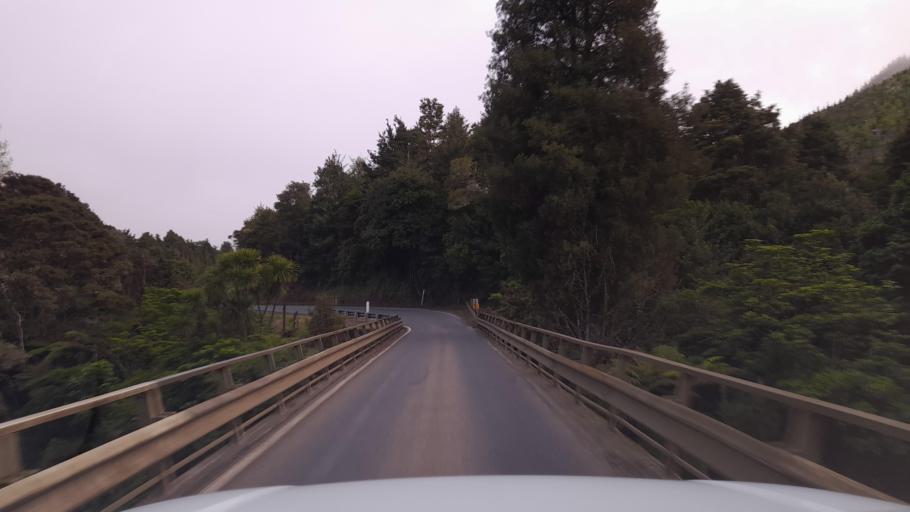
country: NZ
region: Northland
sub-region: Far North District
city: Moerewa
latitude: -35.6238
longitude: 173.8467
